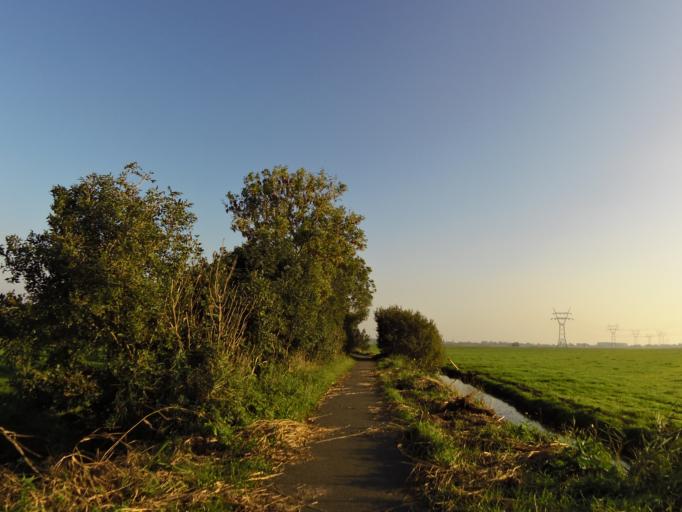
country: NL
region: South Holland
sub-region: Gemeente Leiderdorp
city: Leiderdorp
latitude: 52.1526
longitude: 4.5721
